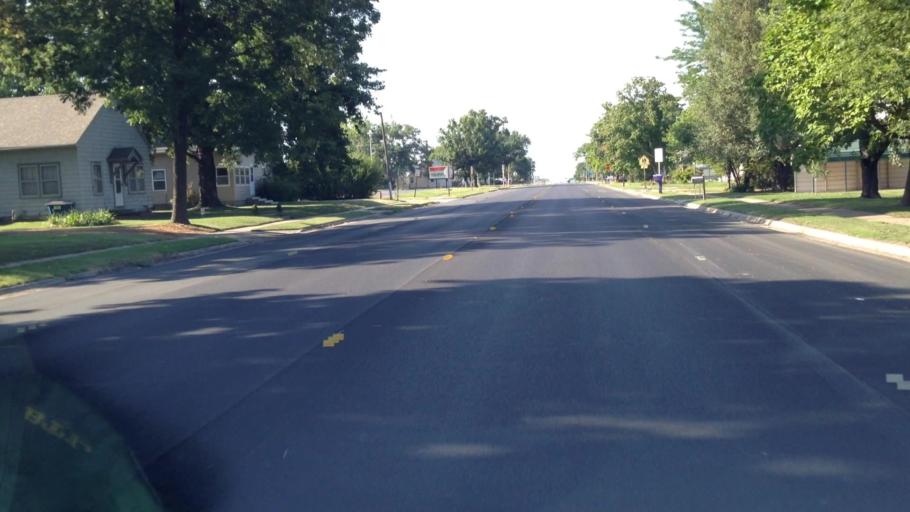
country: US
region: Kansas
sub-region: Allen County
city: Iola
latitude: 37.9180
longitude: -95.1701
